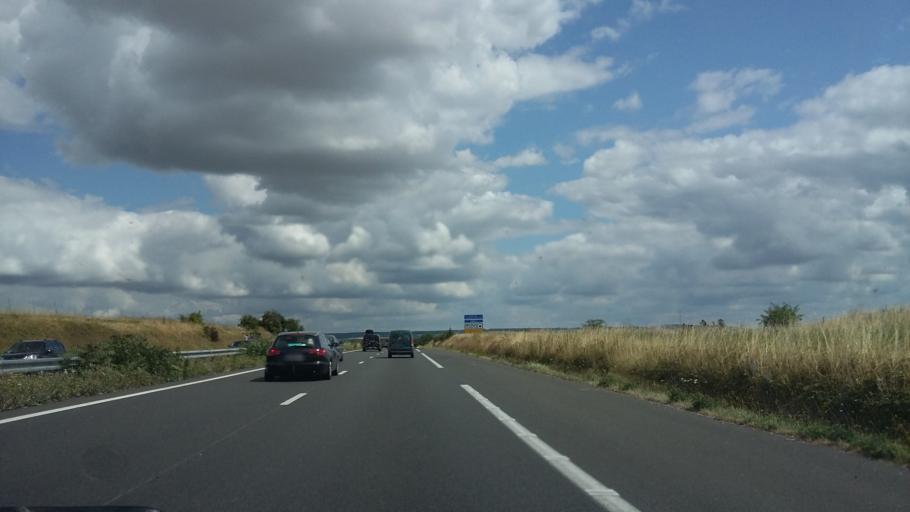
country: FR
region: Poitou-Charentes
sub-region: Departement de la Vienne
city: Jaunay-Clan
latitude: 46.6872
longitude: 0.3637
